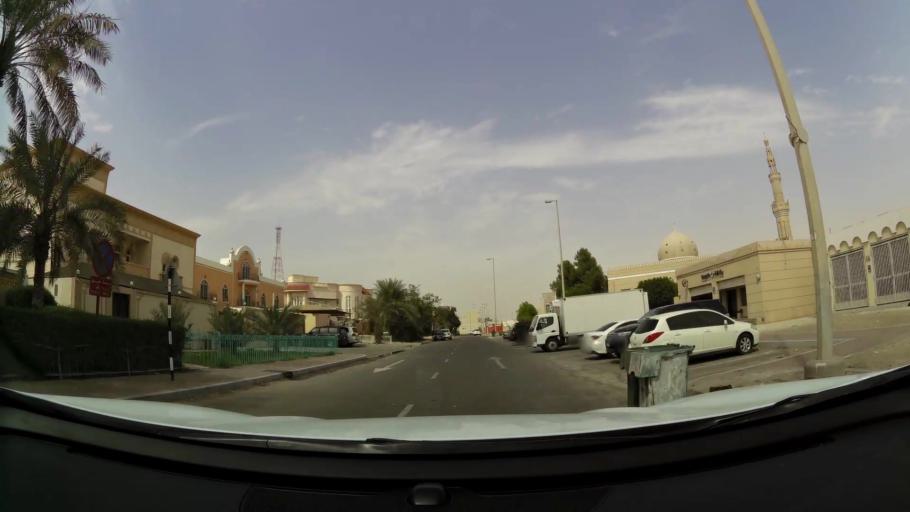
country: AE
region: Abu Dhabi
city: Abu Dhabi
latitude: 24.3116
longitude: 54.6093
